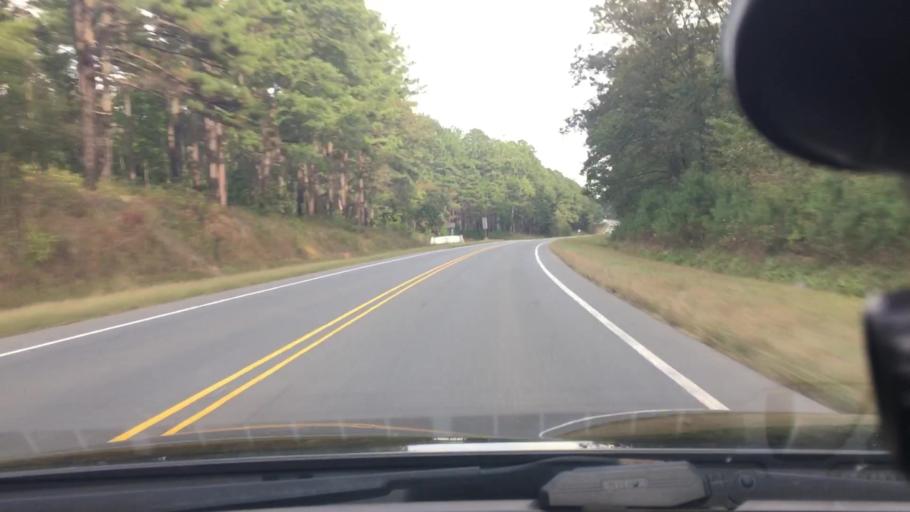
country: US
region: North Carolina
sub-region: Montgomery County
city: Troy
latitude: 35.3226
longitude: -79.9554
